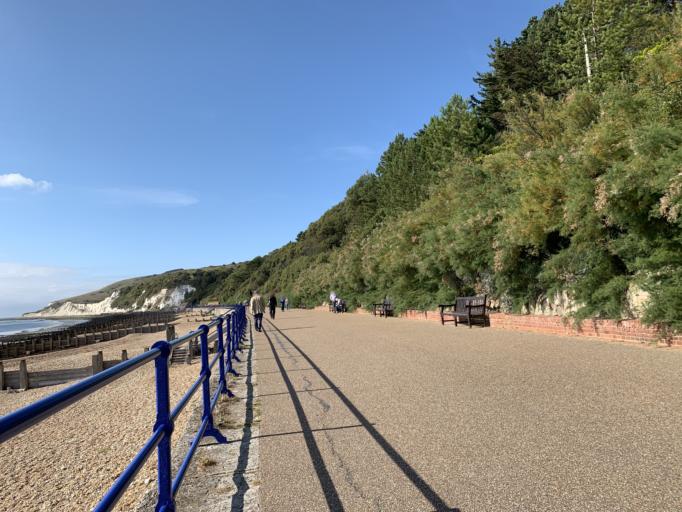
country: GB
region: England
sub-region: East Sussex
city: Eastbourne
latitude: 50.7567
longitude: 0.2781
